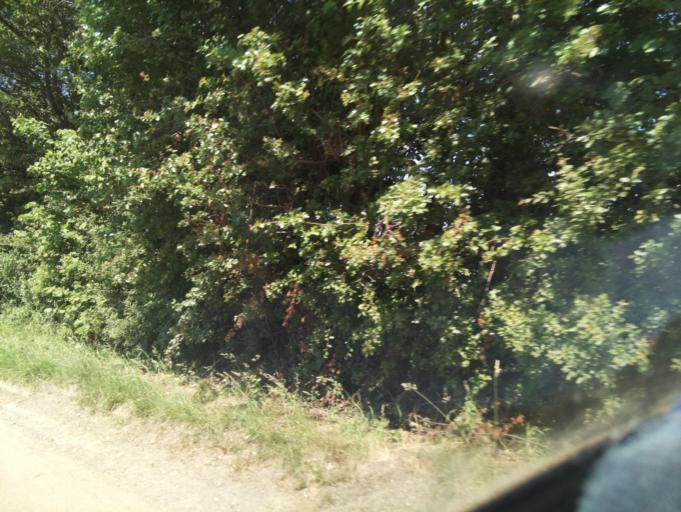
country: GB
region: England
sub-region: Wiltshire
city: Bremhill
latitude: 51.4584
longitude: -2.0652
